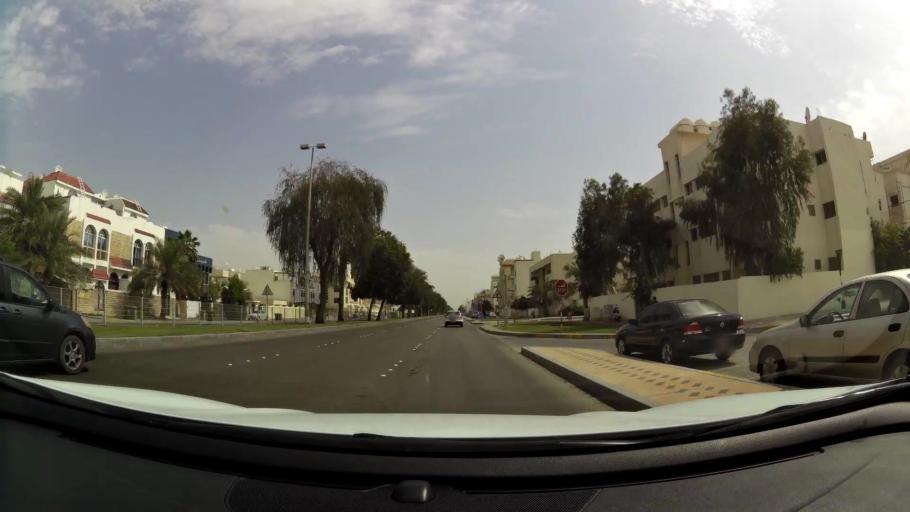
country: AE
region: Abu Dhabi
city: Abu Dhabi
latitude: 24.4604
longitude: 54.3625
